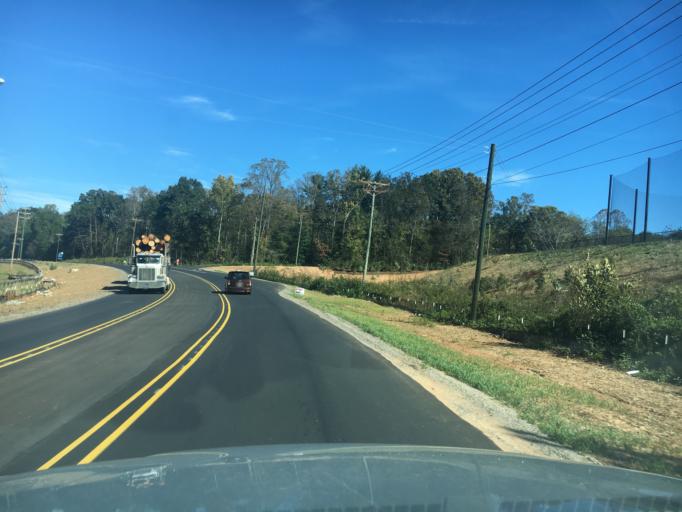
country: US
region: North Carolina
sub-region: Burke County
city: Morganton
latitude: 35.7545
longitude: -81.7034
